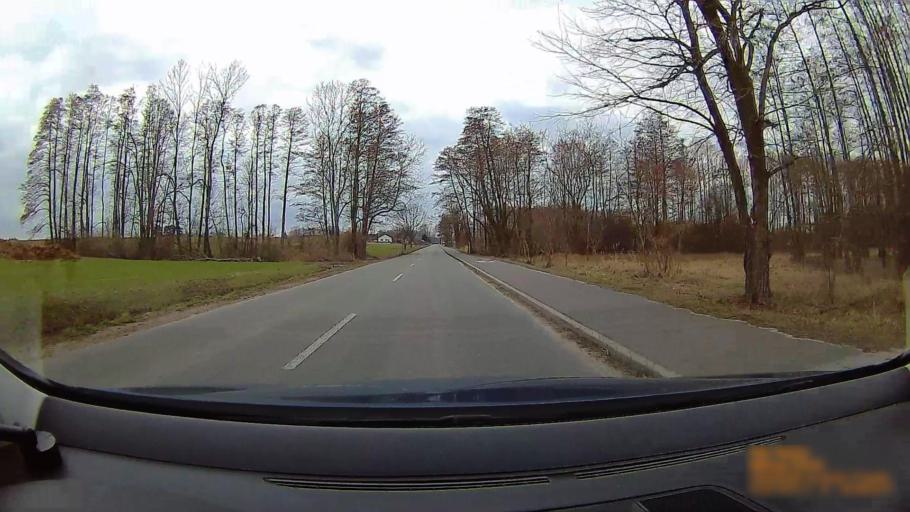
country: PL
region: Greater Poland Voivodeship
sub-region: Powiat koninski
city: Rzgow Pierwszy
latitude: 52.1741
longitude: 18.0920
